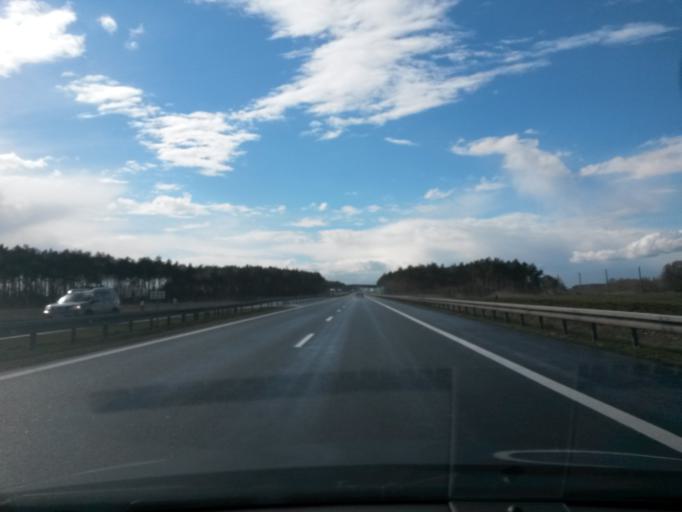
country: PL
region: Greater Poland Voivodeship
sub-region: Powiat slupecki
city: Strzalkowo
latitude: 52.2630
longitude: 17.7664
